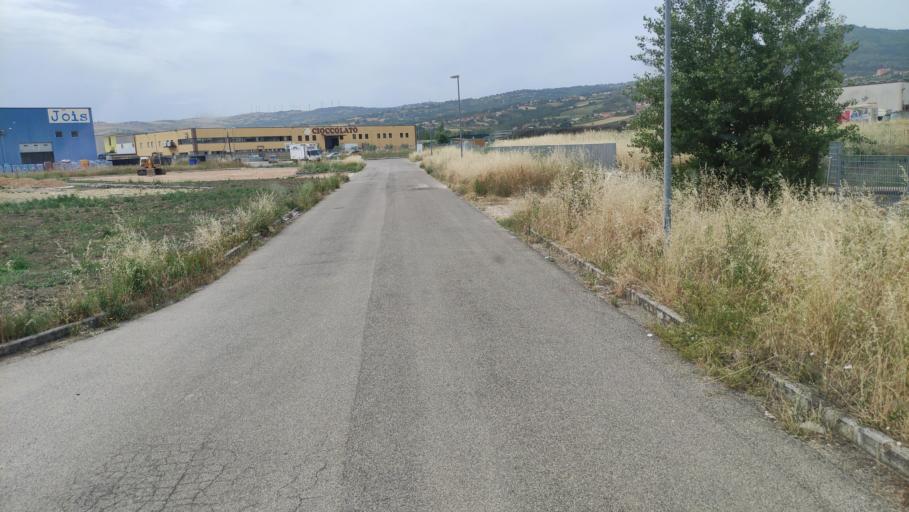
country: IT
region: Campania
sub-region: Provincia di Avellino
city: Sturno
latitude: 41.0501
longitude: 15.1218
